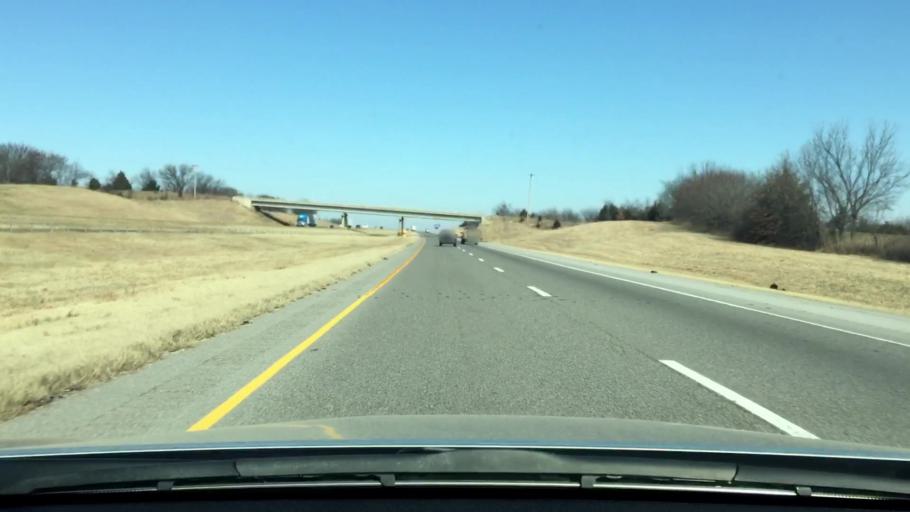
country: US
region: Oklahoma
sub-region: McClain County
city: Purcell
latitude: 34.9548
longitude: -97.3686
